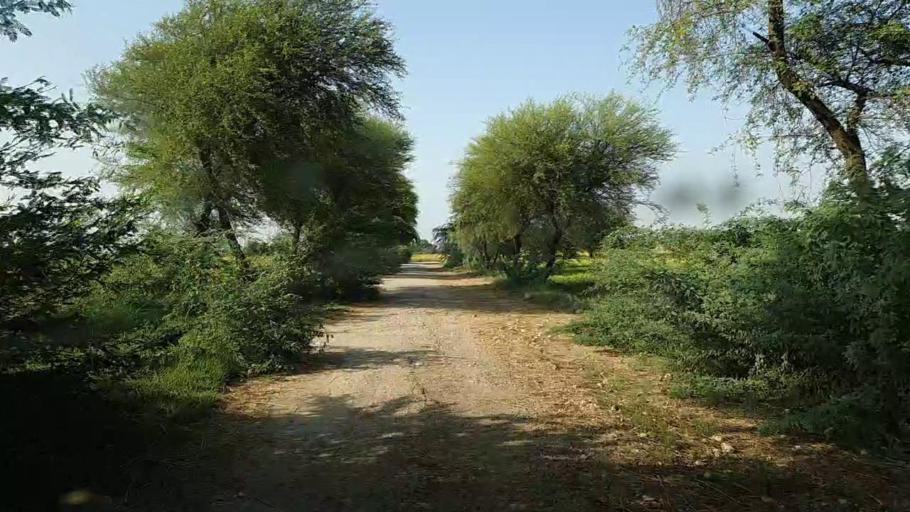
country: PK
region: Sindh
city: Bulri
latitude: 24.7804
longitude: 68.4335
